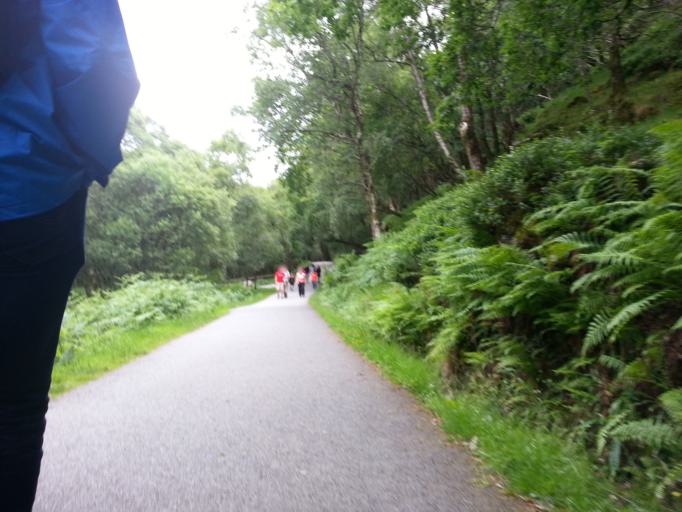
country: IE
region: Leinster
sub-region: Wicklow
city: Rathdrum
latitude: 53.0055
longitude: -6.3432
